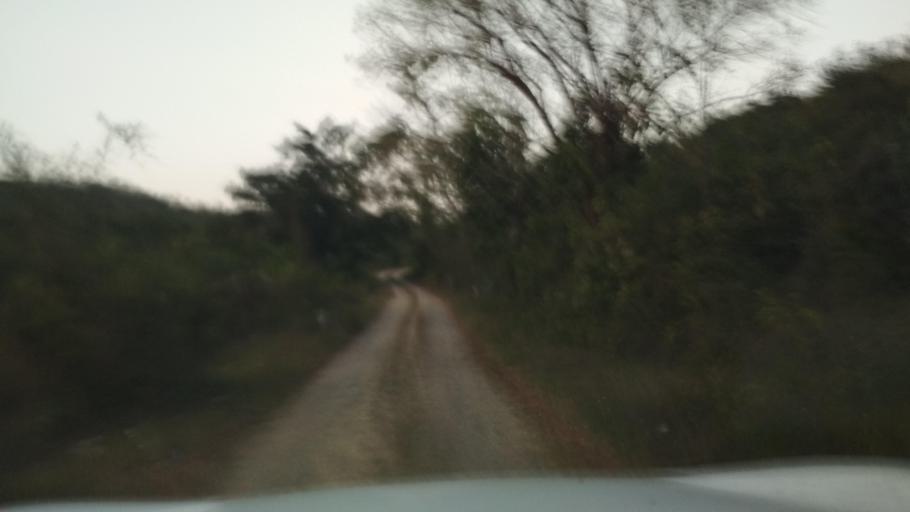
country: MX
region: Veracruz
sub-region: Poza Rica de Hidalgo
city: Arroyo del Maiz Uno
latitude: 20.4822
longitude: -97.3900
